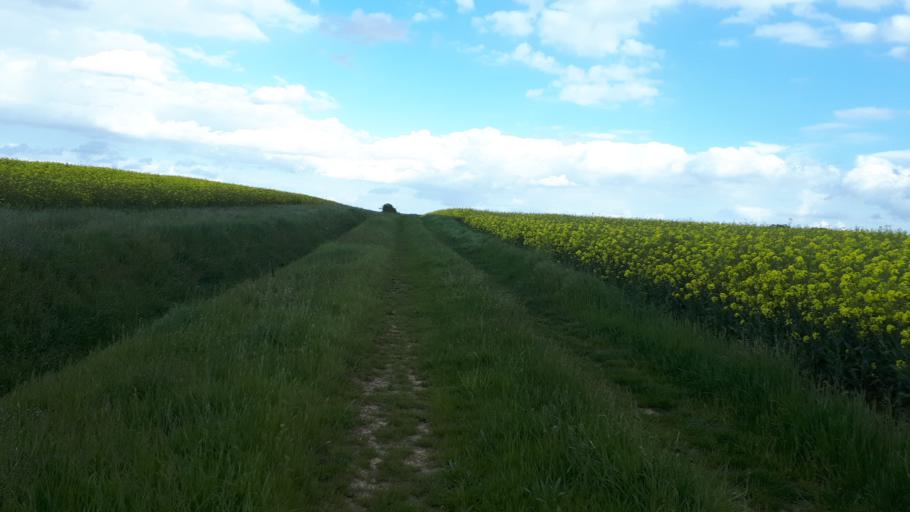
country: FR
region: Centre
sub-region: Departement du Loir-et-Cher
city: Aze
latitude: 47.8342
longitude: 1.0020
